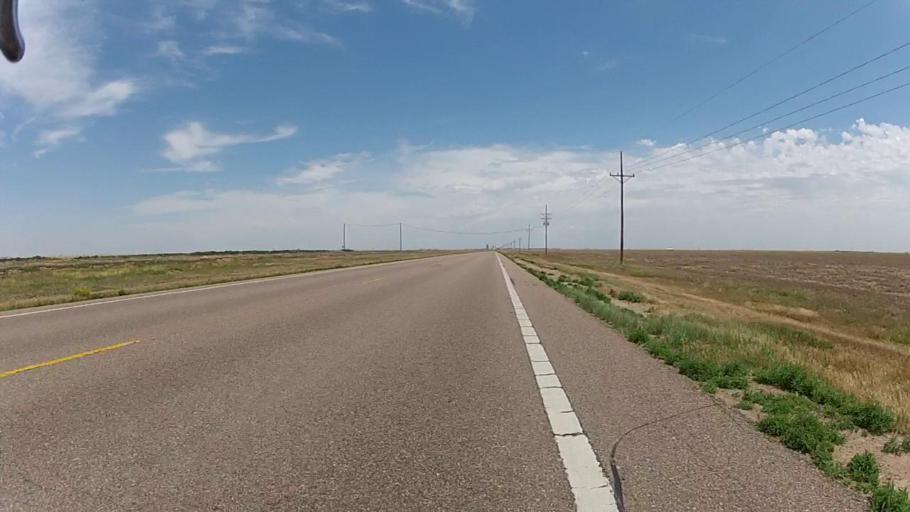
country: US
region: Kansas
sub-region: Haskell County
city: Satanta
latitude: 37.4627
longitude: -100.9180
